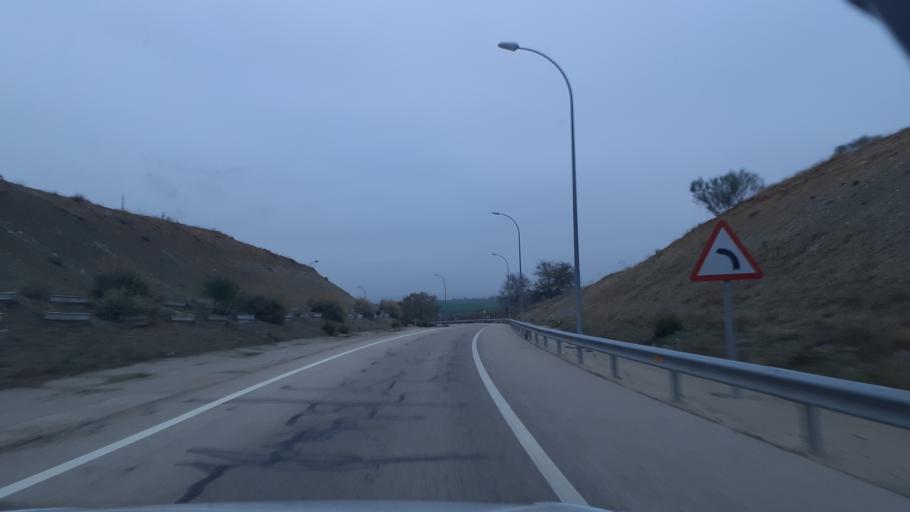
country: ES
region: Madrid
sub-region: Provincia de Madrid
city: Paracuellos de Jarama
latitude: 40.4826
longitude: -3.4967
